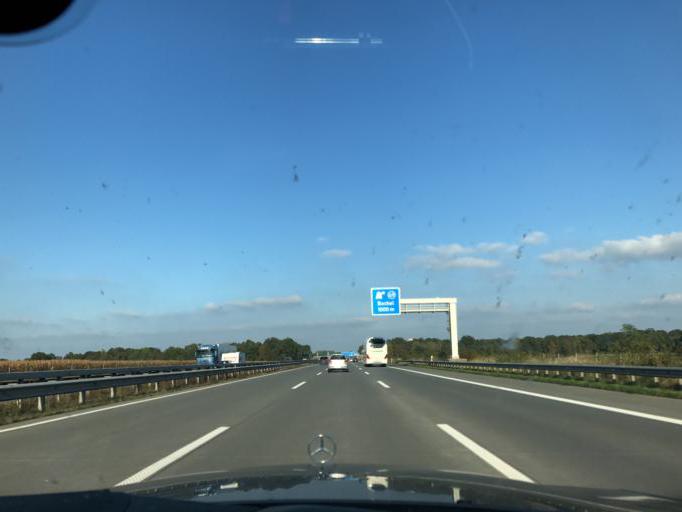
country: DE
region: Lower Saxony
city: Horstedt
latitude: 53.1837
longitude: 9.2711
